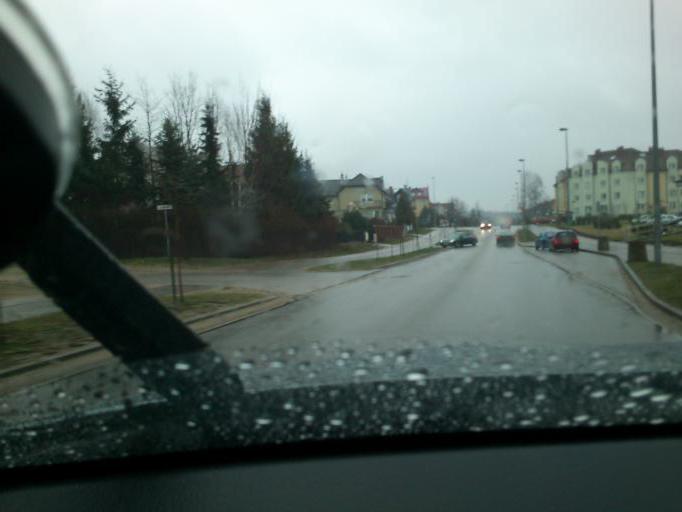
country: PL
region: Pomeranian Voivodeship
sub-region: Gdynia
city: Wielki Kack
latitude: 54.4247
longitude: 18.4766
